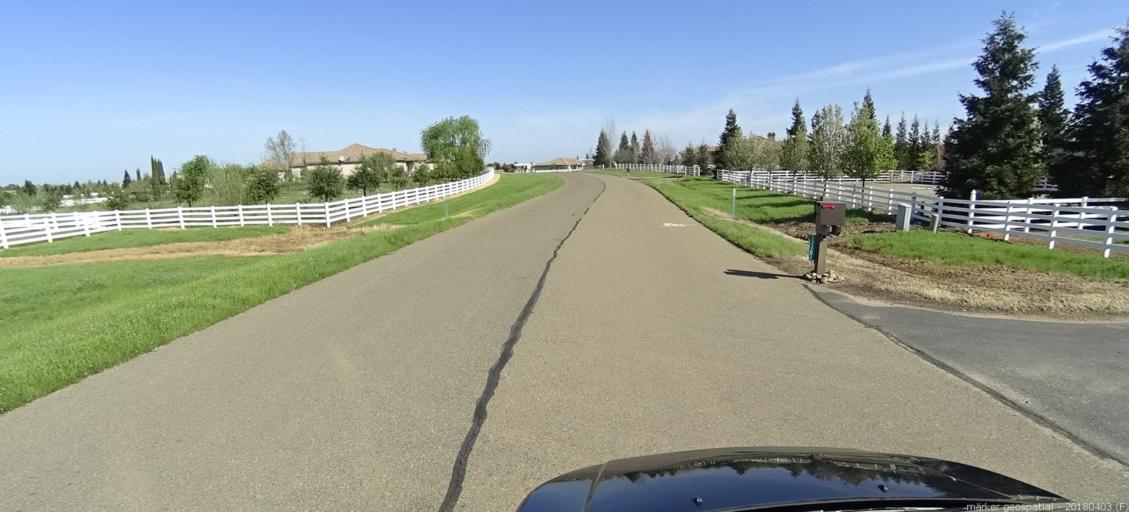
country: US
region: California
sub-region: Sacramento County
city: Wilton
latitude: 38.4117
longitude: -121.1955
